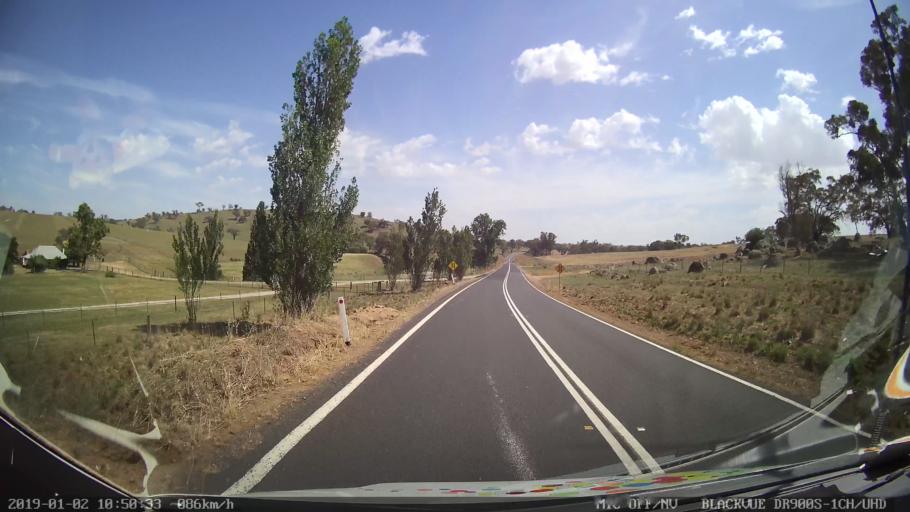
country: AU
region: New South Wales
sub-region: Cootamundra
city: Cootamundra
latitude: -34.7135
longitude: 148.2761
